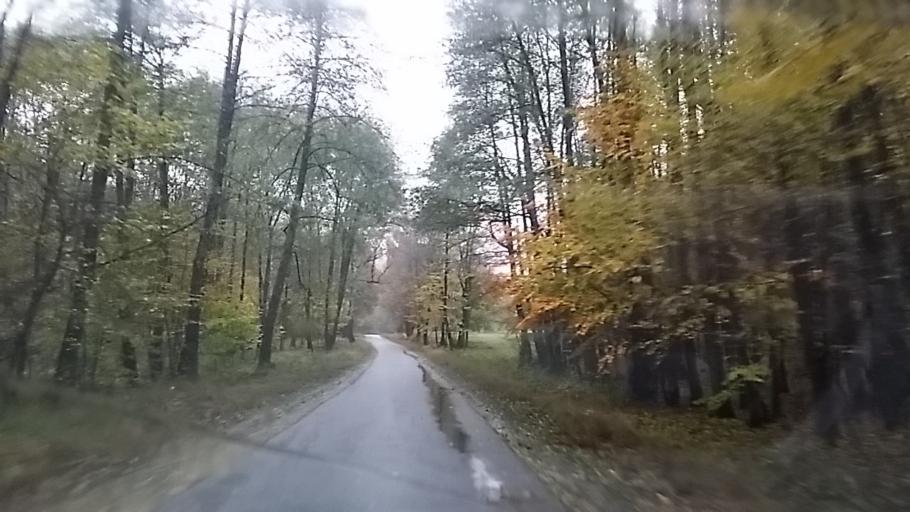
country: HU
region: Borsod-Abauj-Zemplen
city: Tolcsva
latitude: 48.4404
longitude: 21.4606
